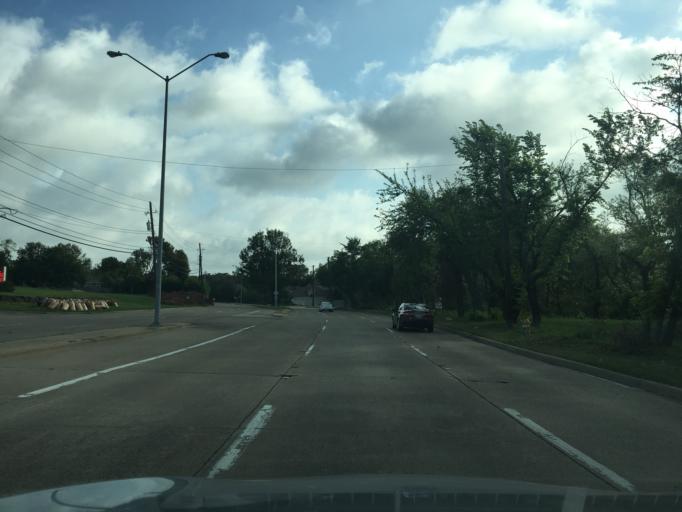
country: US
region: Texas
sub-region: Dallas County
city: Richardson
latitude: 32.8959
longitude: -96.7515
